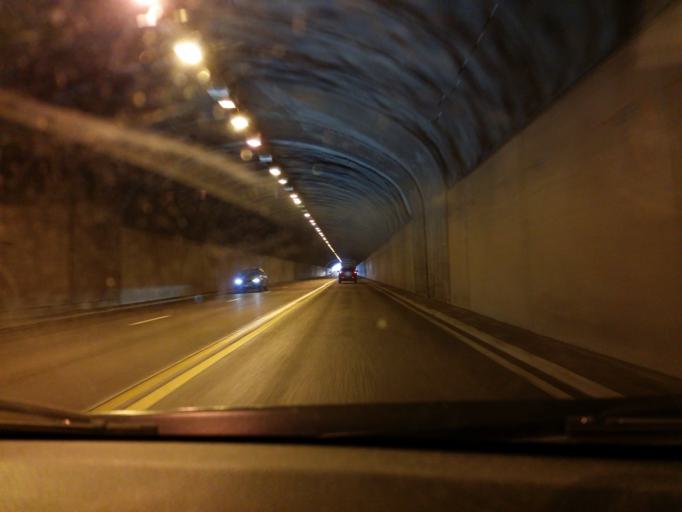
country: NO
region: Buskerud
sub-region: Hole
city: Vik
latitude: 59.9793
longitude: 10.3200
